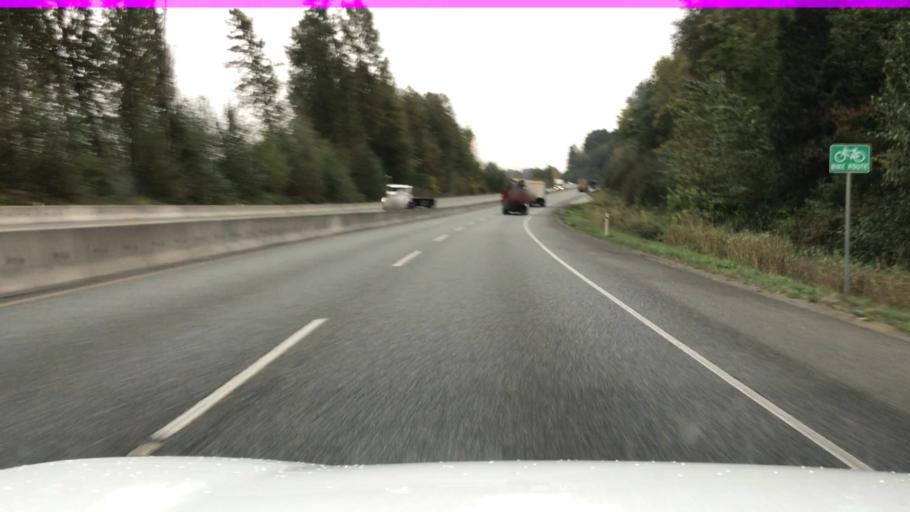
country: CA
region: British Columbia
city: Coquitlam
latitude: 49.2119
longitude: -122.7890
